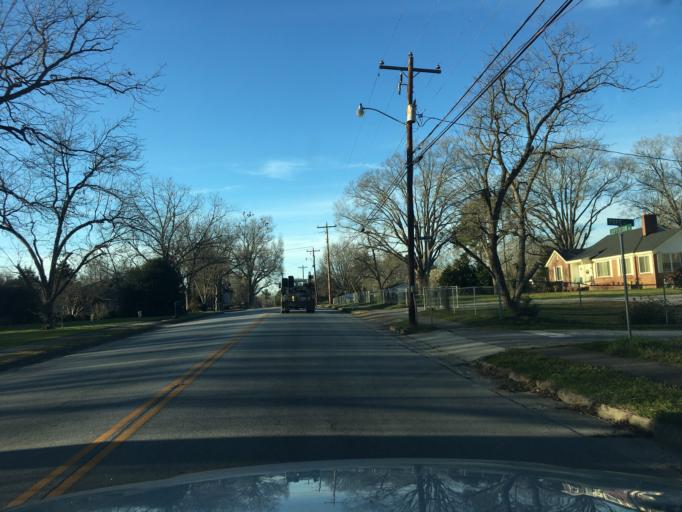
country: US
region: South Carolina
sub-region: Saluda County
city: Saluda
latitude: 34.0084
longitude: -81.7750
